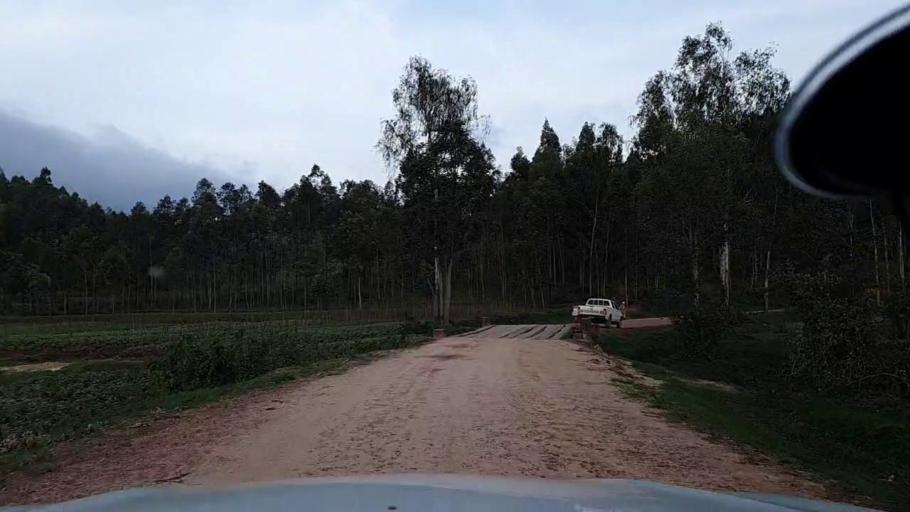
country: RW
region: Southern Province
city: Gitarama
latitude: -2.2090
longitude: 29.6164
